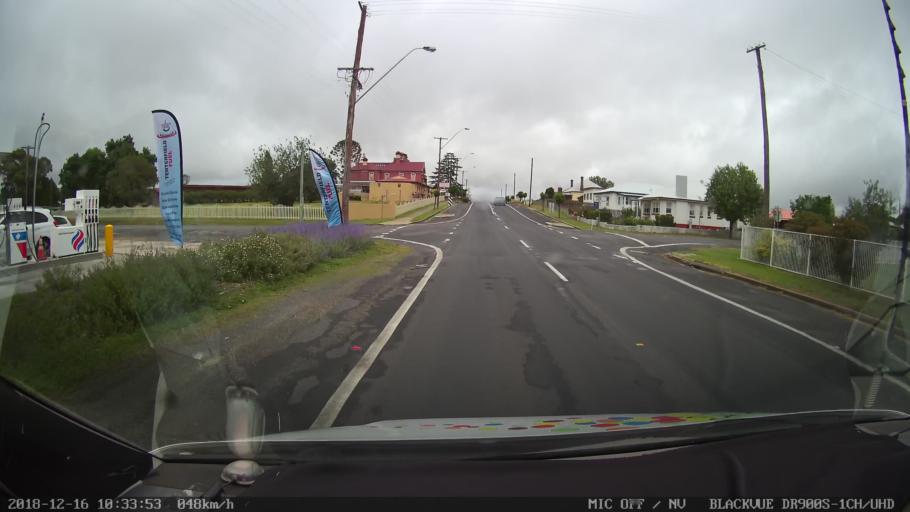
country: AU
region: New South Wales
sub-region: Tenterfield Municipality
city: Carrolls Creek
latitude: -29.0618
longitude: 152.0176
